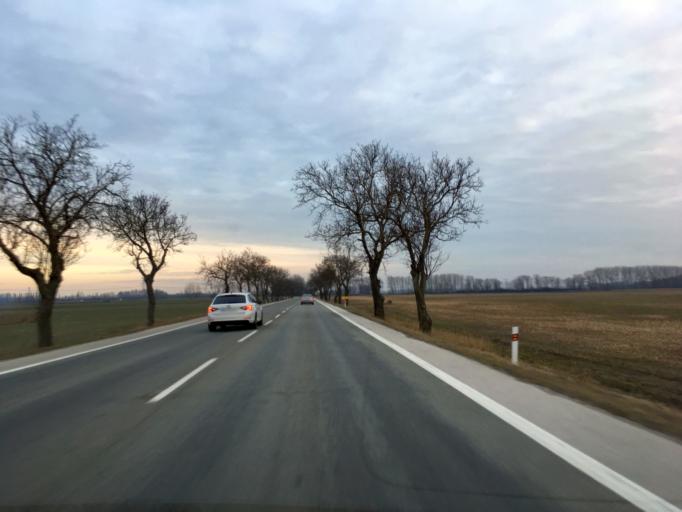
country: SK
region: Trnavsky
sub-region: Okres Dunajska Streda
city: Velky Meder
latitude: 47.8936
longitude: 17.7417
